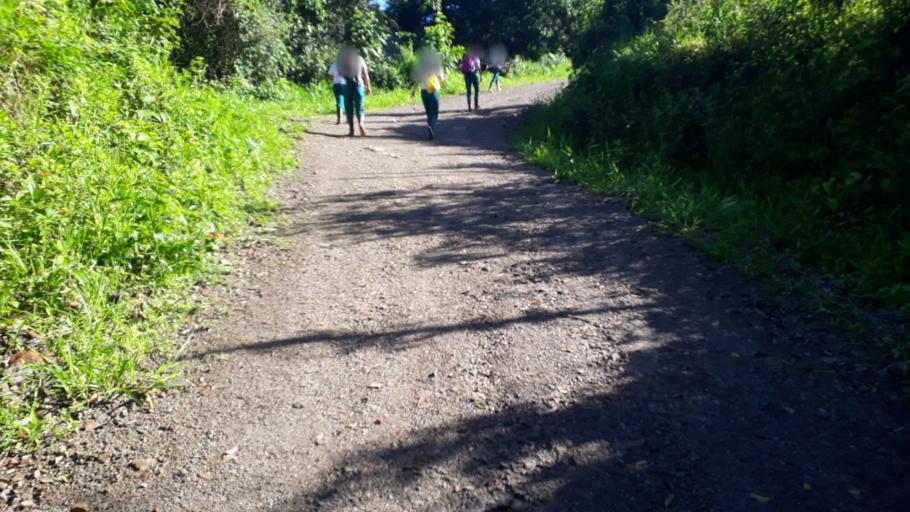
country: CO
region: Casanare
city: Nunchia
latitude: 5.6499
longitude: -72.4237
